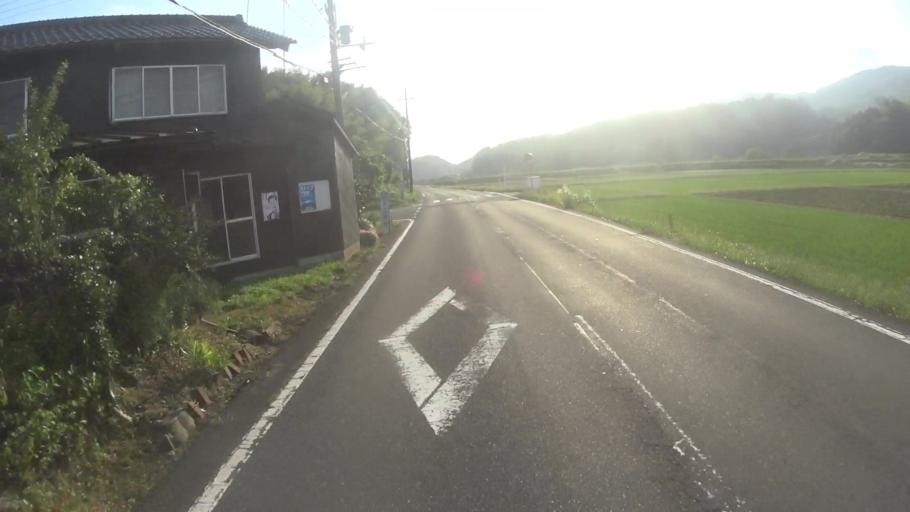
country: JP
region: Kyoto
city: Miyazu
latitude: 35.6929
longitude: 135.1008
